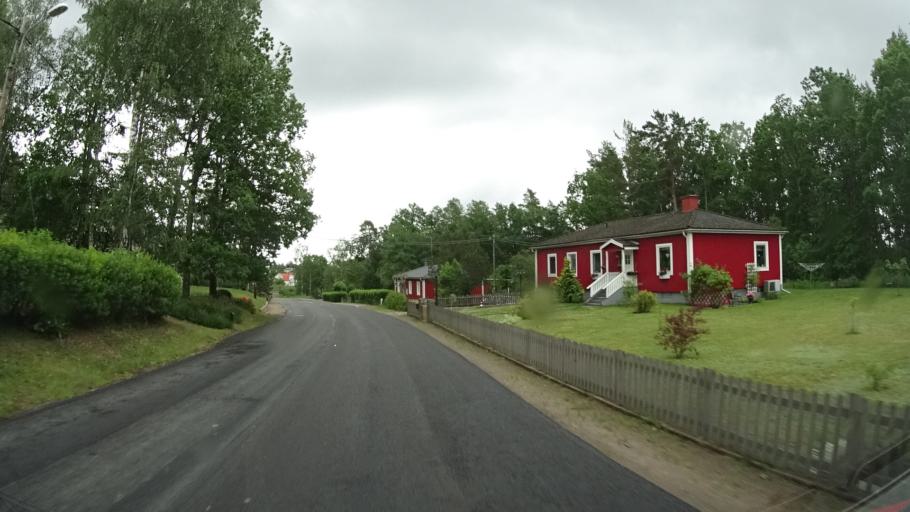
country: SE
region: Kalmar
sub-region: Hogsby Kommun
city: Hoegsby
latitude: 57.4028
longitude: 16.1869
